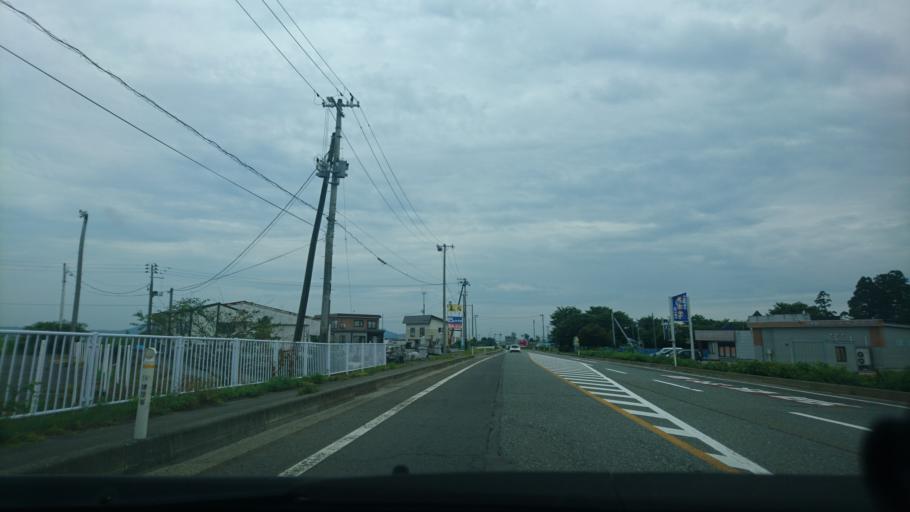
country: JP
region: Akita
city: Omagari
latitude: 39.4180
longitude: 140.5413
